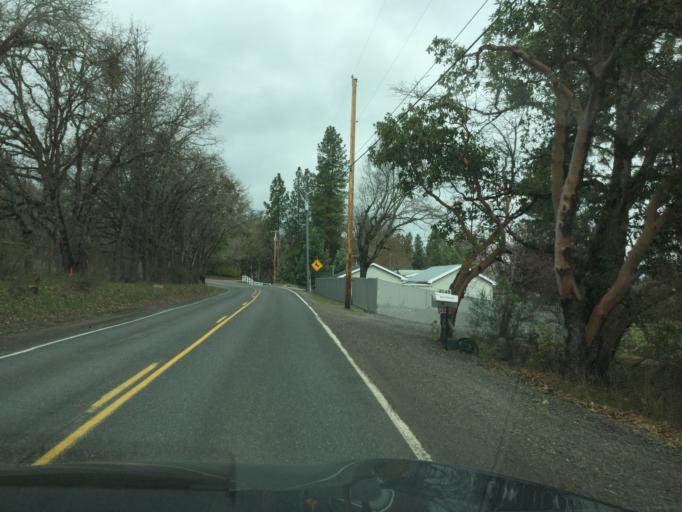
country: US
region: Oregon
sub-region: Jackson County
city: Central Point
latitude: 42.3756
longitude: -122.9539
